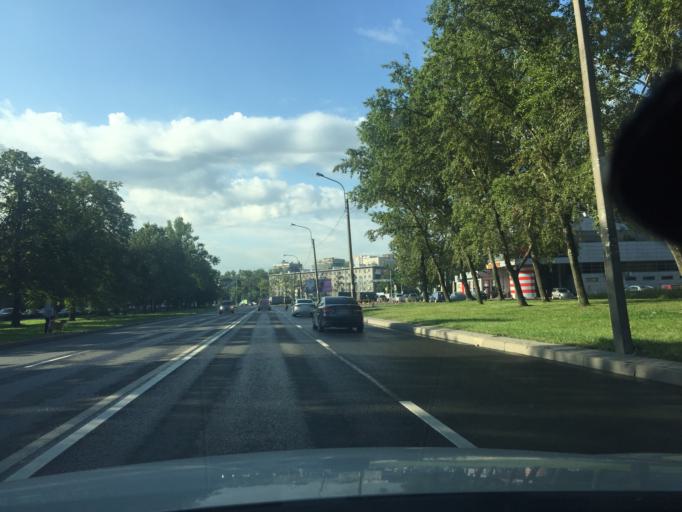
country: RU
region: St.-Petersburg
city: Kupchino
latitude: 59.8413
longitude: 30.3382
